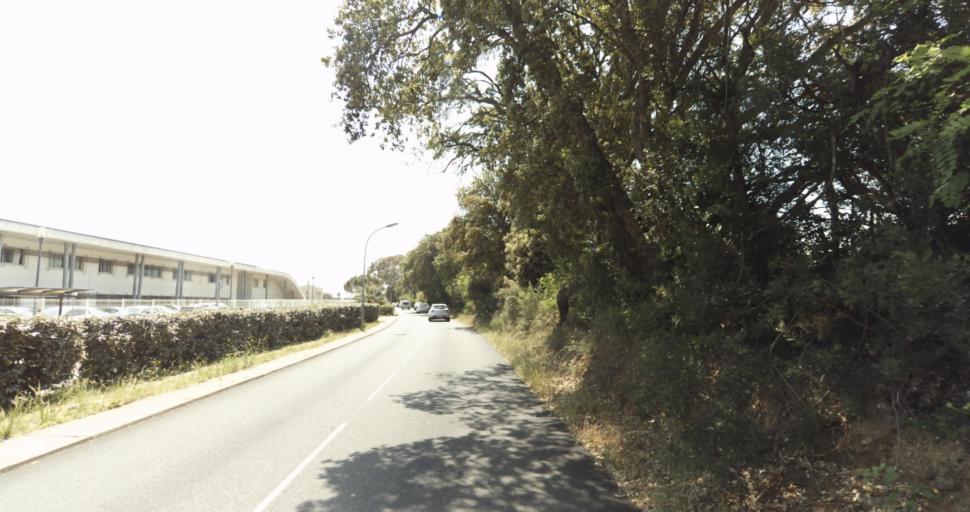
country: FR
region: Corsica
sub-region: Departement de la Haute-Corse
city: Biguglia
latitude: 42.5979
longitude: 9.4358
